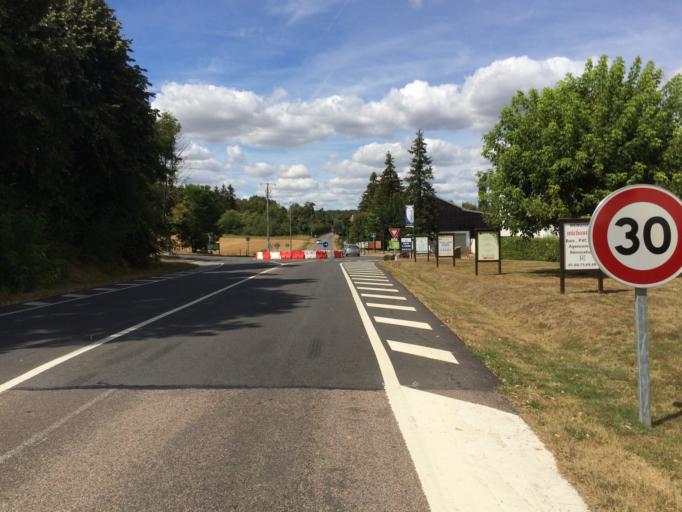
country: FR
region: Ile-de-France
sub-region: Departement de l'Essonne
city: Maisse
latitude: 48.3522
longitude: 2.3808
